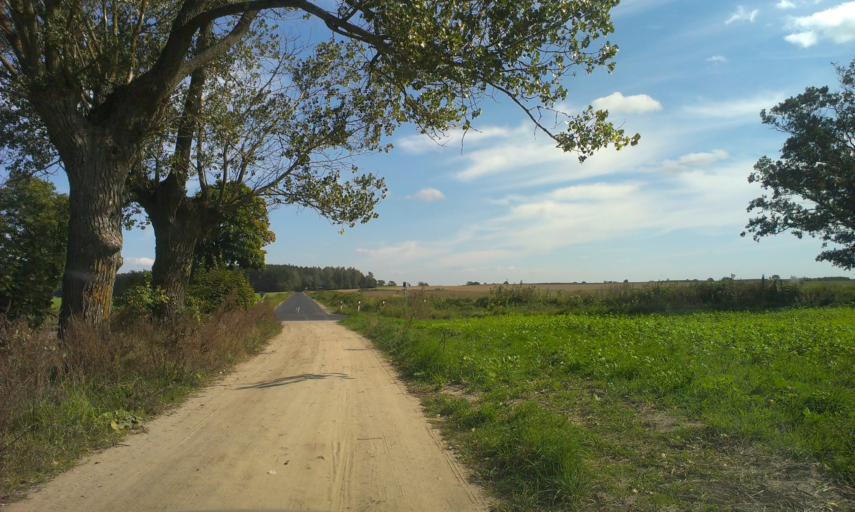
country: PL
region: Greater Poland Voivodeship
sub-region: Powiat pilski
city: Lobzenica
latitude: 53.2846
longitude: 17.1770
